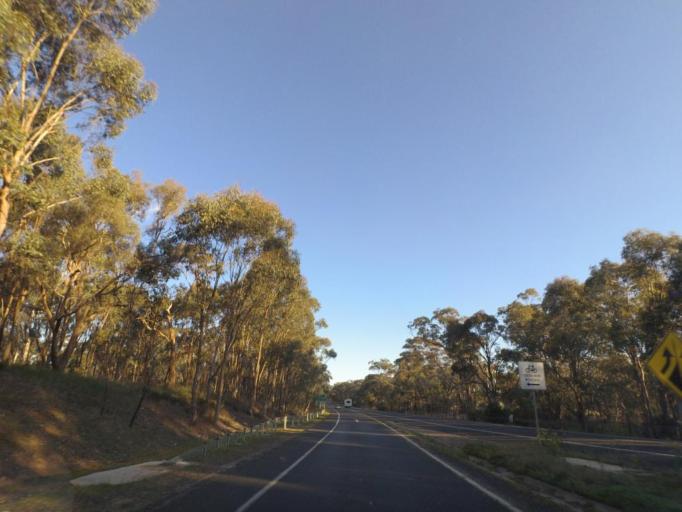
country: AU
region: Victoria
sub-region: Murrindindi
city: Kinglake West
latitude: -37.0673
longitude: 145.1018
